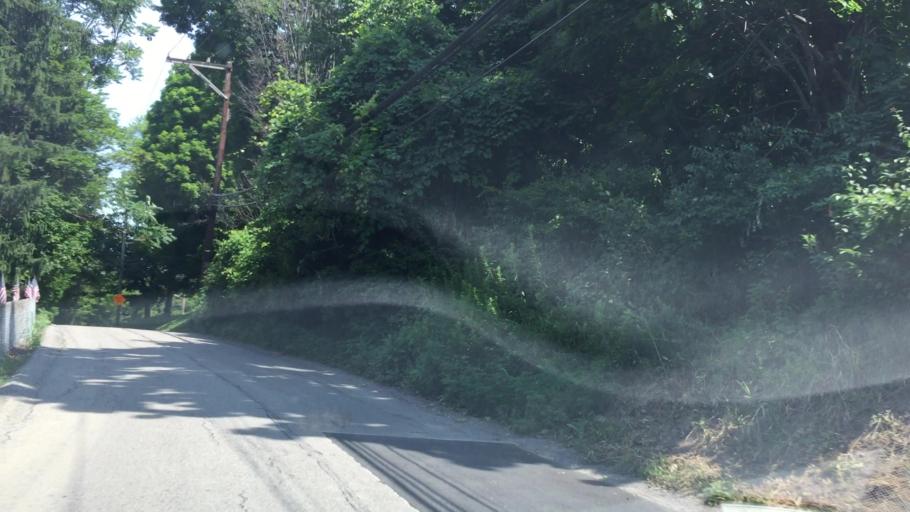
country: US
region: Pennsylvania
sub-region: Allegheny County
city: West View
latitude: 40.5019
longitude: -80.0095
